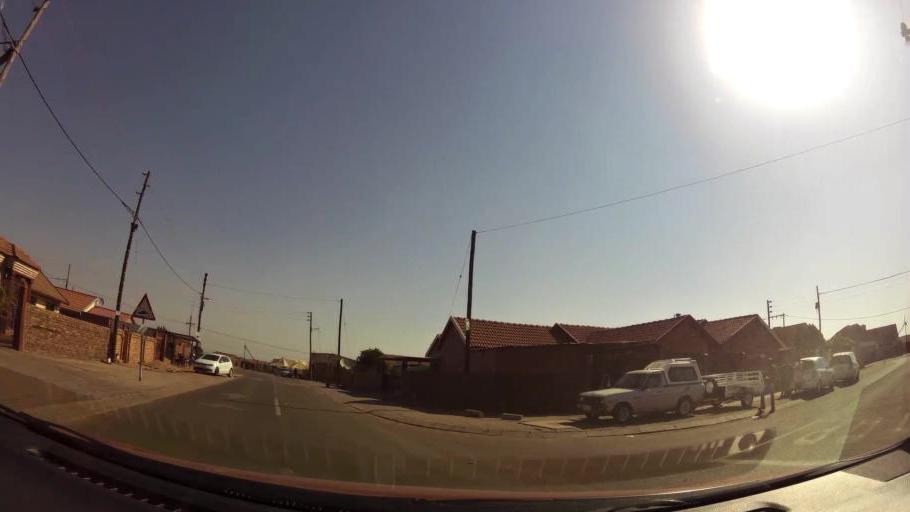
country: ZA
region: Gauteng
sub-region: City of Tshwane Metropolitan Municipality
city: Mabopane
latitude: -25.5543
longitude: 28.0811
